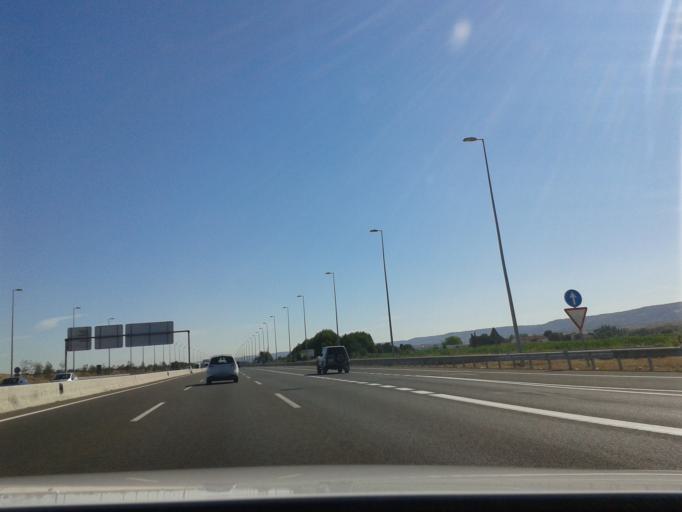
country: ES
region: Madrid
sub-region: Provincia de Madrid
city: Meco
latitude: 40.5132
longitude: -3.3176
